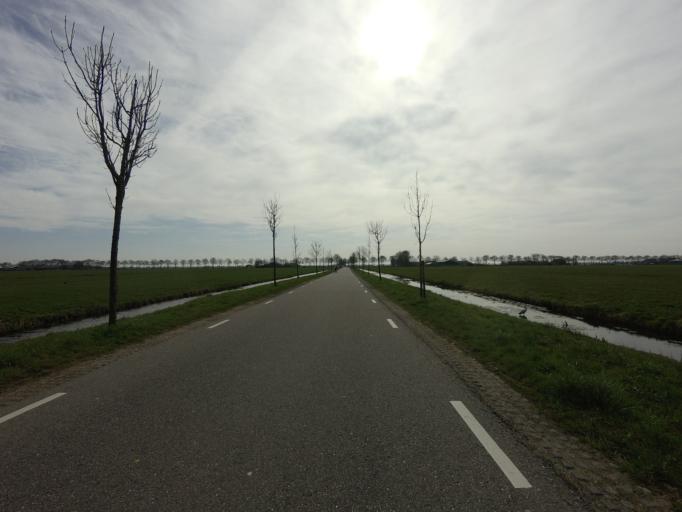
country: NL
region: South Holland
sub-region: Gemeente Alphen aan den Rijn
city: Alphen aan den Rijn
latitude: 52.1068
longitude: 4.6883
